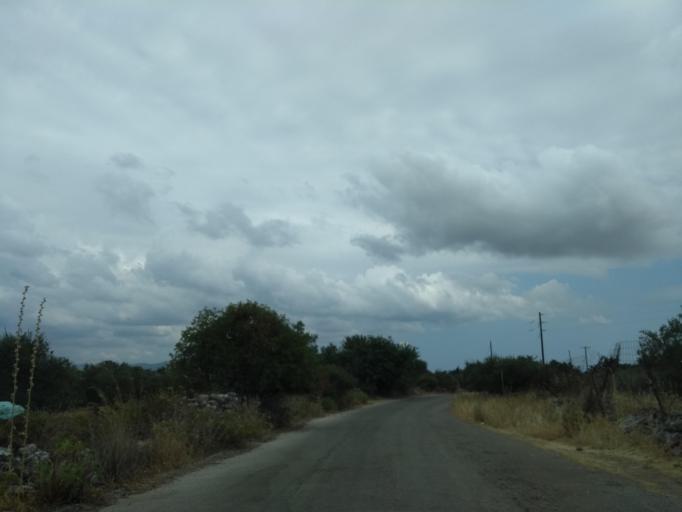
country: GR
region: Crete
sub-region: Nomos Chanias
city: Georgioupolis
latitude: 35.3961
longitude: 24.2298
